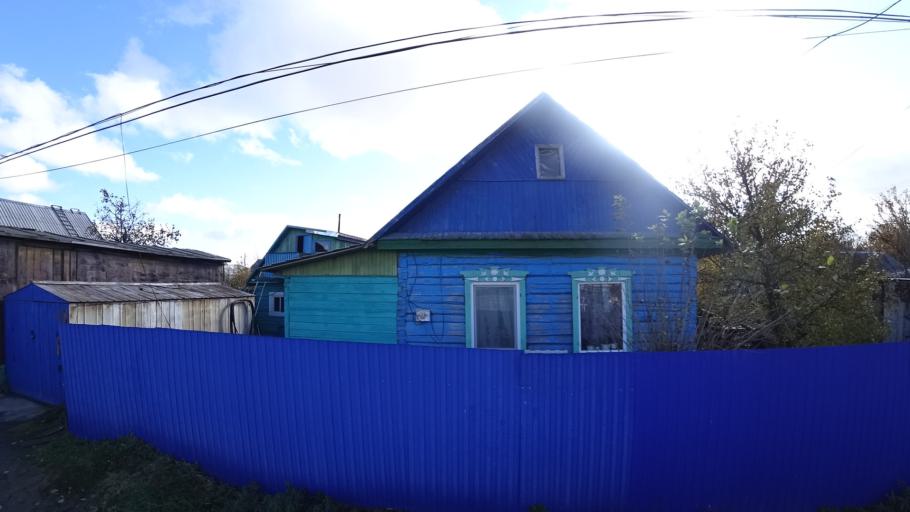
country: RU
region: Khabarovsk Krai
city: Amursk
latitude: 50.2334
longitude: 136.9185
